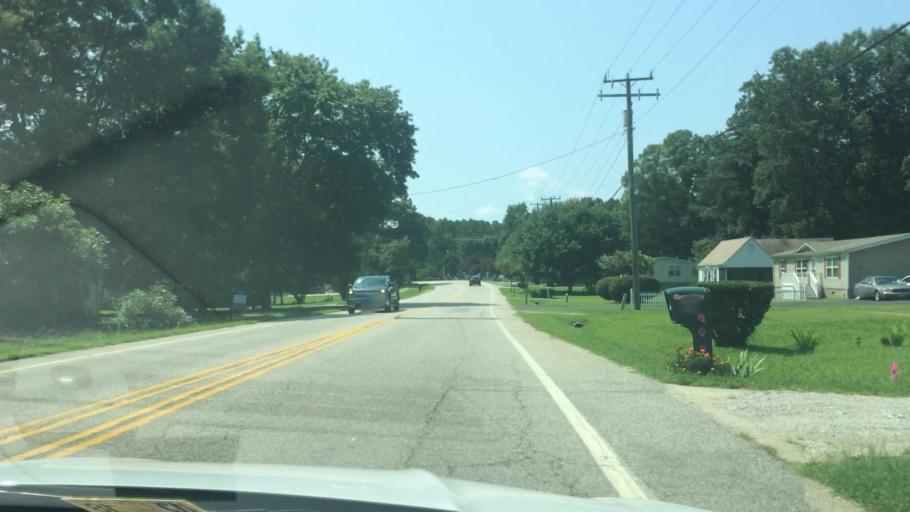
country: US
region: Virginia
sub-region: James City County
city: Williamsburg
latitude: 37.3260
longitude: -76.7894
